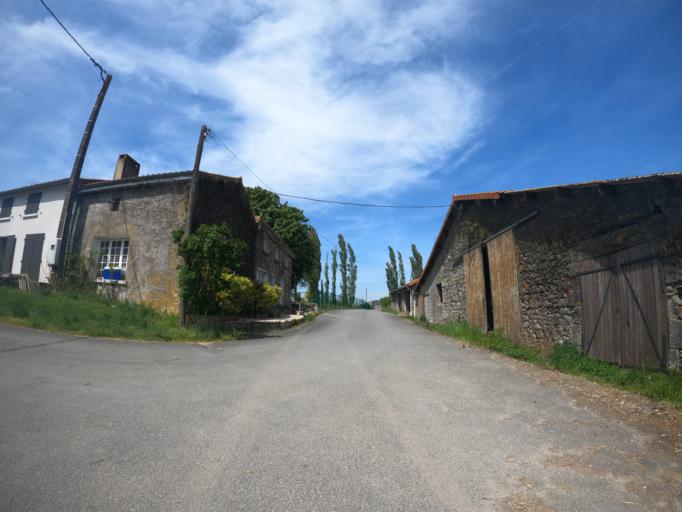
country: FR
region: Poitou-Charentes
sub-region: Departement des Deux-Sevres
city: Secondigny
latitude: 46.6463
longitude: -0.4922
